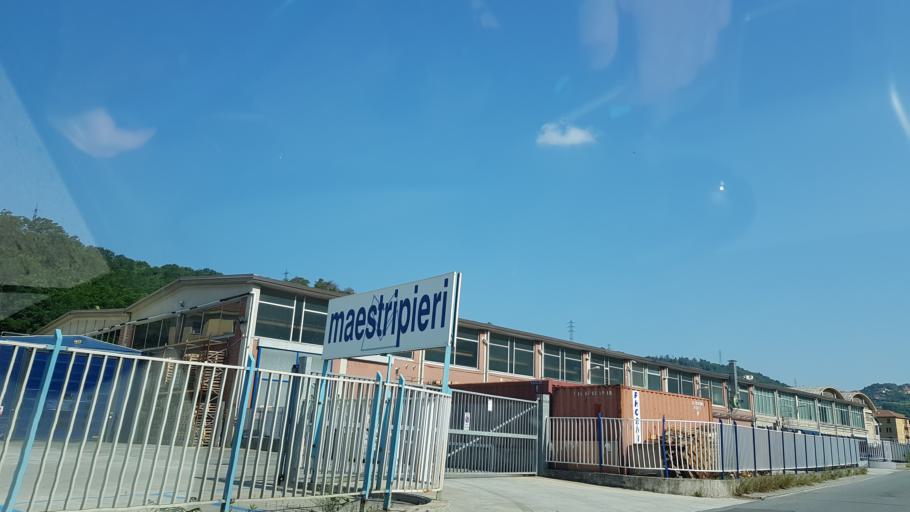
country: IT
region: Liguria
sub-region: Provincia di Genova
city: Manesseno
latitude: 44.4871
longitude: 8.9214
